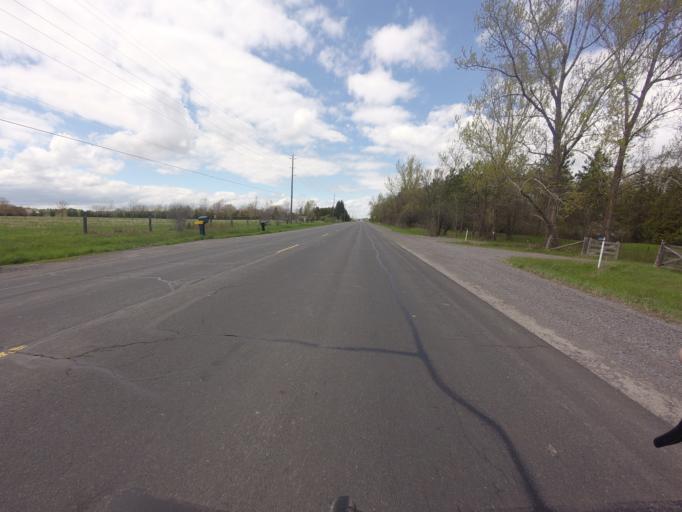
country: CA
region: Ontario
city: Carleton Place
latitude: 45.2458
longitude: -76.2374
